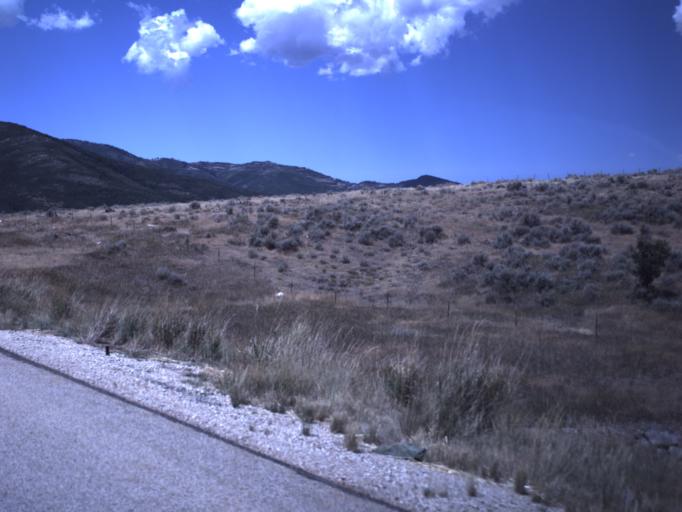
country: US
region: Utah
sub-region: Wasatch County
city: Heber
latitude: 40.5944
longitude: -111.4082
